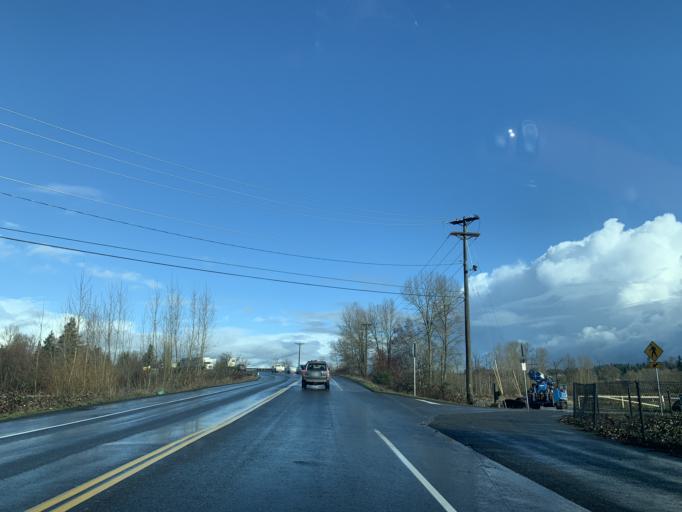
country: US
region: Washington
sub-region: Pierce County
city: Fife Heights
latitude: 47.2414
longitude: -122.3361
